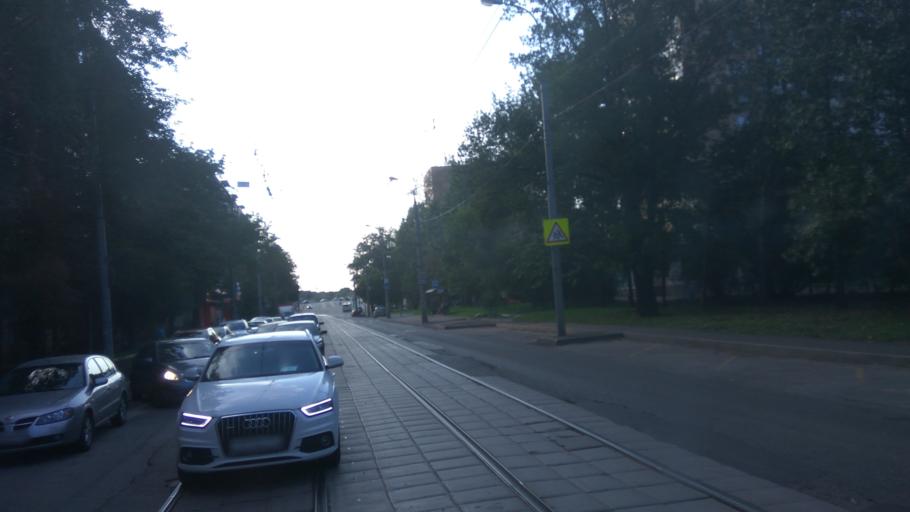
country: RU
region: Moskovskaya
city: Koptevo
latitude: 55.8391
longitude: 37.5288
